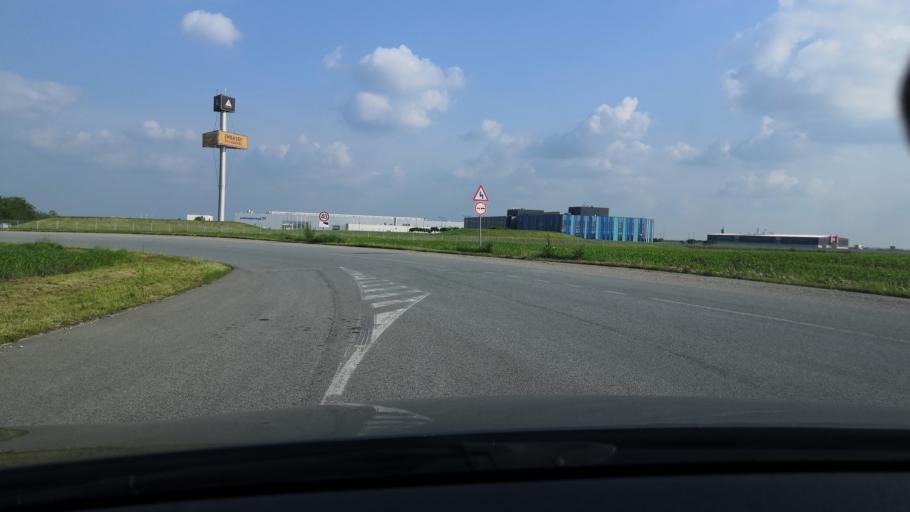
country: RS
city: Beska
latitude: 45.0975
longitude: 20.0916
